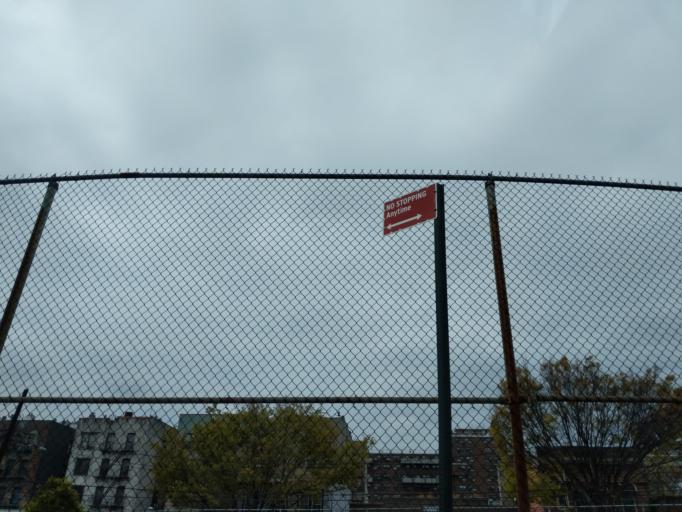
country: US
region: New York
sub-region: Bronx
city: The Bronx
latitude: 40.8551
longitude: -73.8949
